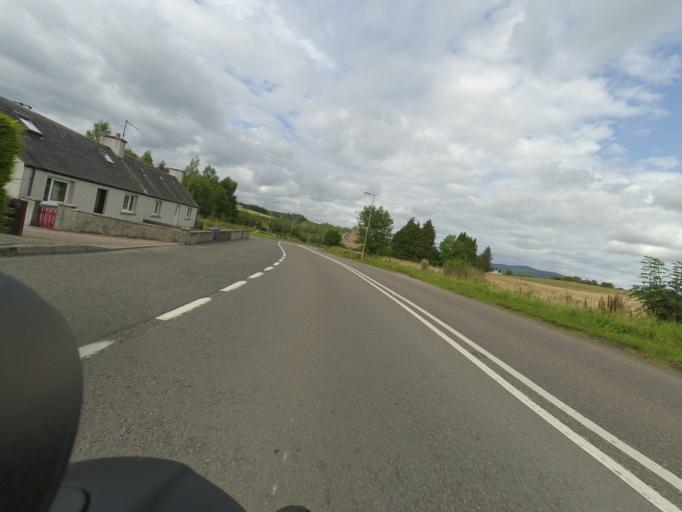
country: GB
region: Scotland
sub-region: Moray
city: Rothes
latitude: 57.4620
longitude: -3.2404
